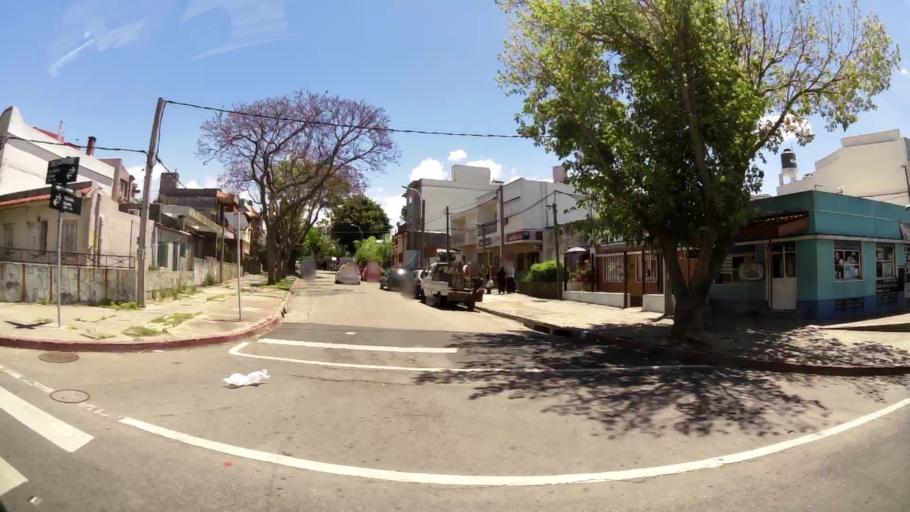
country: UY
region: Montevideo
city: Montevideo
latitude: -34.8941
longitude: -56.1378
